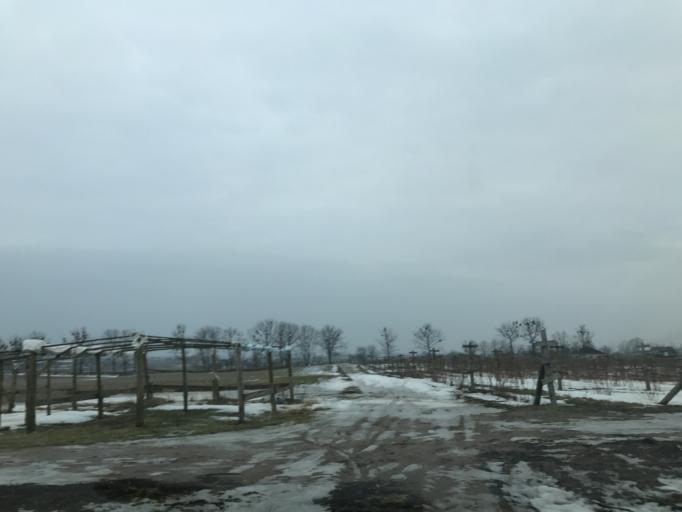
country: PL
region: Kujawsko-Pomorskie
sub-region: Powiat brodnicki
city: Bartniczka
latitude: 53.2263
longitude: 19.6078
